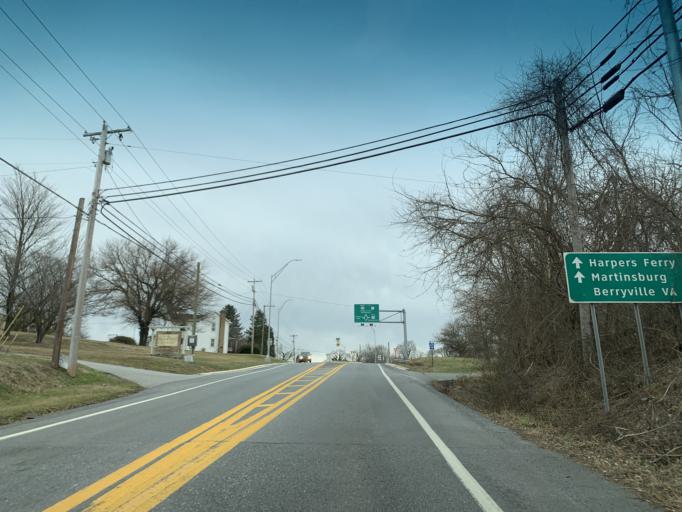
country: US
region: West Virginia
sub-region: Jefferson County
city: Charles Town
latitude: 39.2762
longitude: -77.8503
